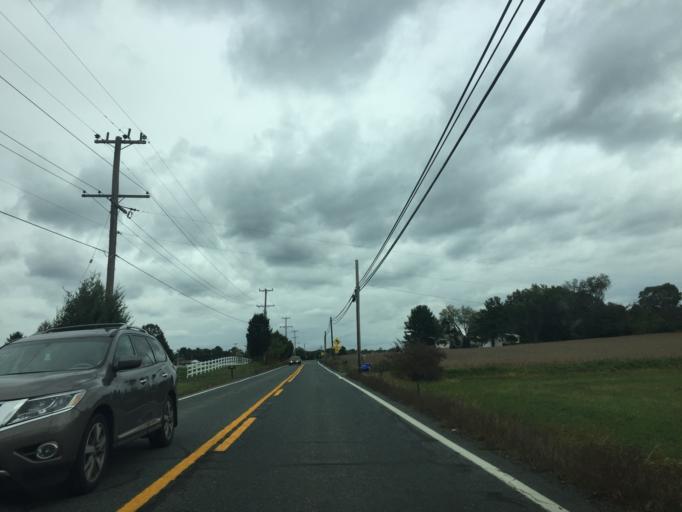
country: US
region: Maryland
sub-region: Harford County
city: Riverside
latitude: 39.5439
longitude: -76.2546
